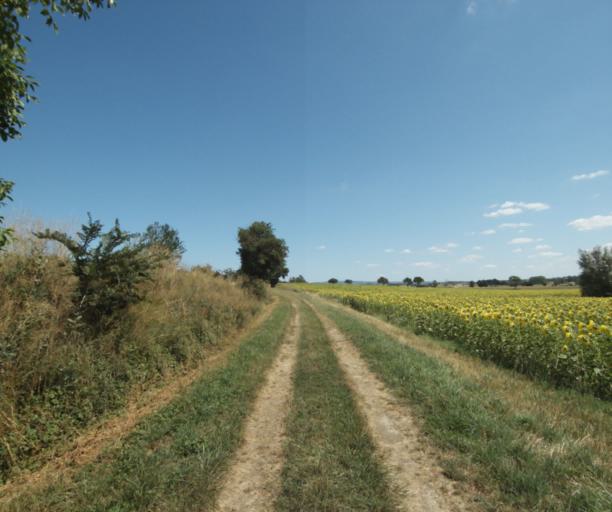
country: FR
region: Midi-Pyrenees
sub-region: Departement de la Haute-Garonne
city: Auriac-sur-Vendinelle
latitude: 43.4977
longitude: 1.8708
